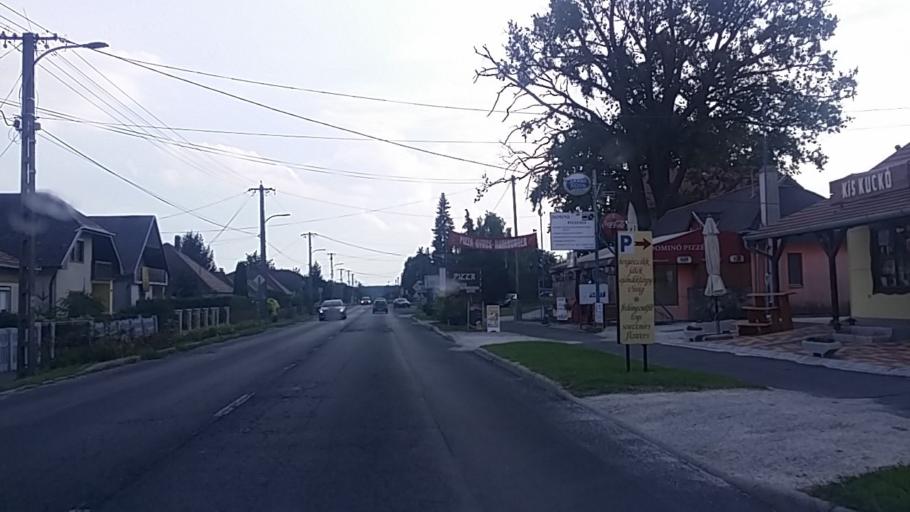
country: HU
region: Zala
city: Sarmellek
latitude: 46.7105
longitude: 17.1691
